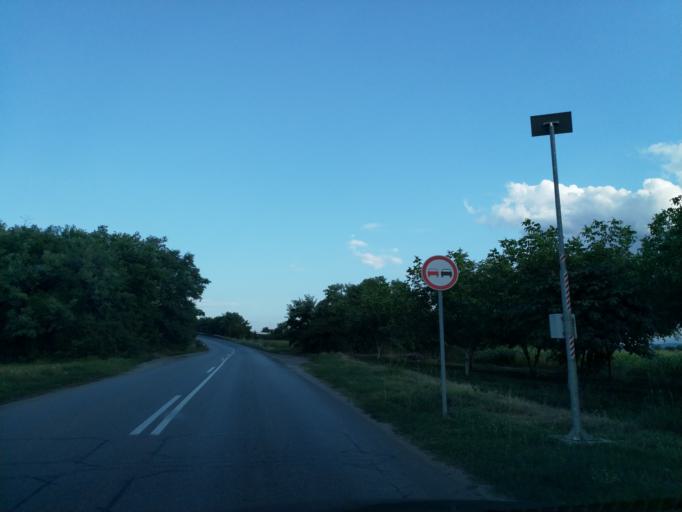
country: RS
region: Central Serbia
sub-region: Rasinski Okrug
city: Cicevac
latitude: 43.7511
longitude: 21.4412
